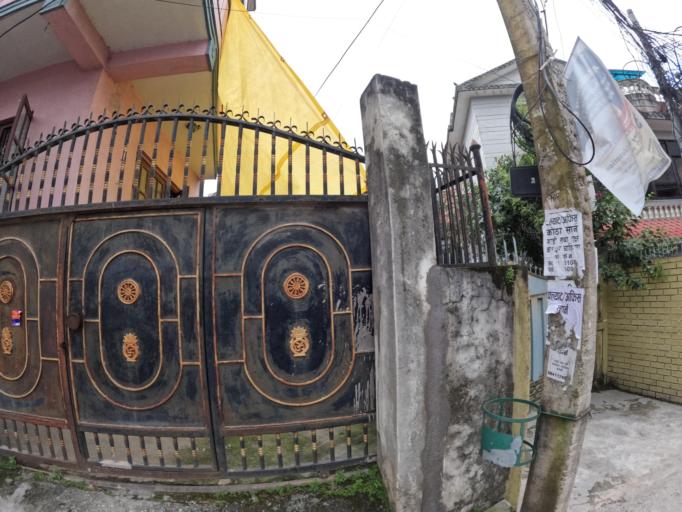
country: NP
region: Central Region
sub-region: Bagmati Zone
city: Kathmandu
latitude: 27.7434
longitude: 85.3201
